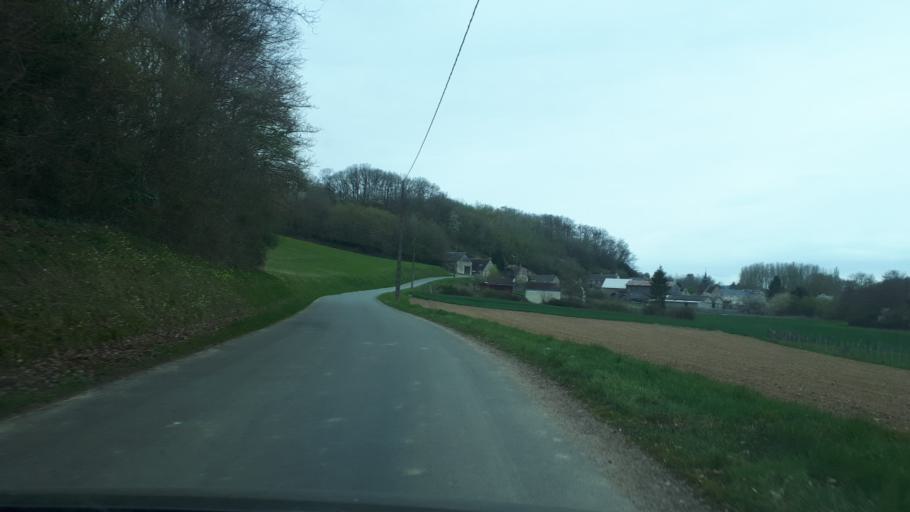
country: FR
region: Centre
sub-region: Departement du Loir-et-Cher
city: Lunay
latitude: 47.7594
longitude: 0.9265
